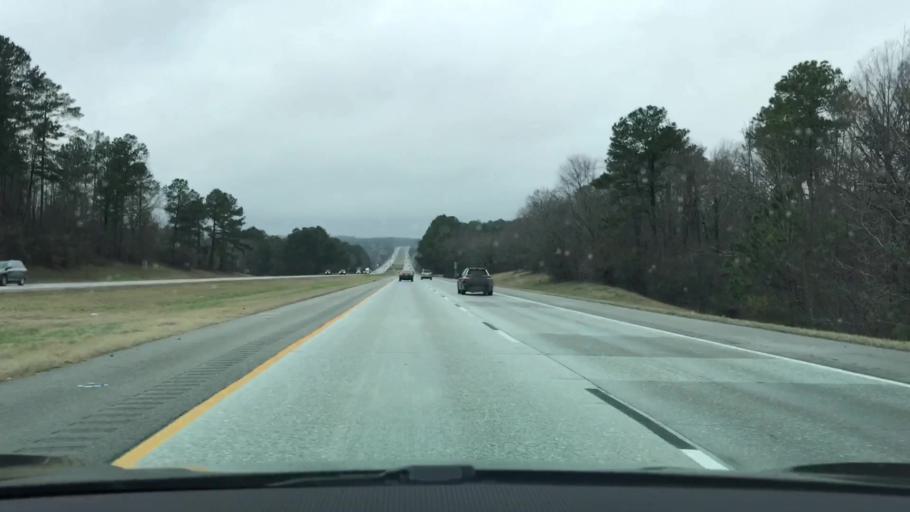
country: US
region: Georgia
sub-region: Greene County
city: Greensboro
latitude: 33.5351
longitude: -83.2595
